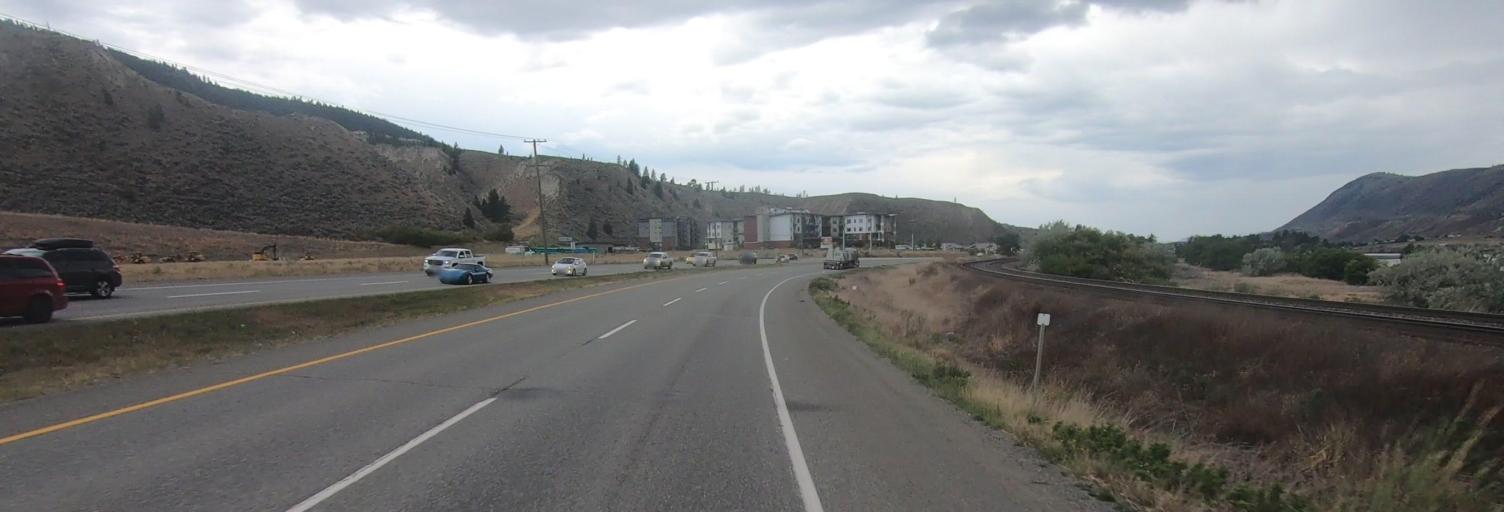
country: CA
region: British Columbia
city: Kamloops
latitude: 50.6713
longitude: -120.2189
